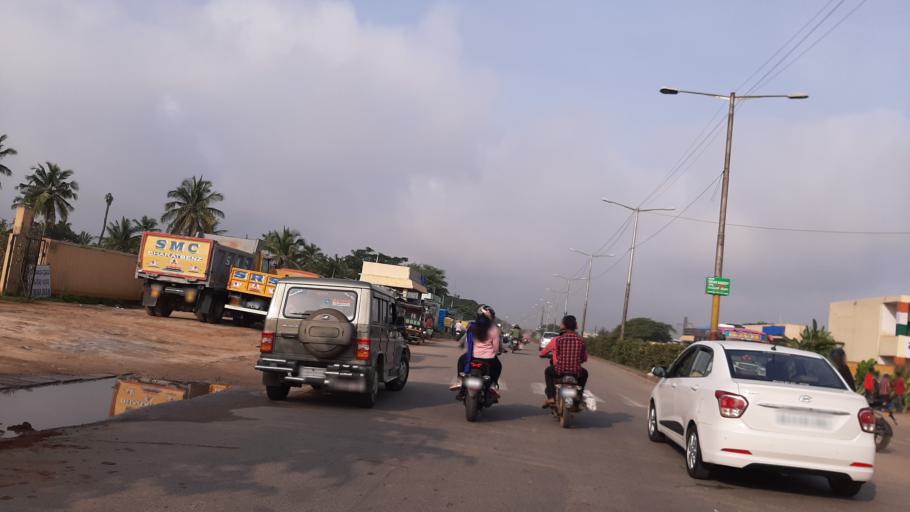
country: IN
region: Karnataka
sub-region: Bangalore Urban
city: Bangalore
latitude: 12.9877
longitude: 77.4940
